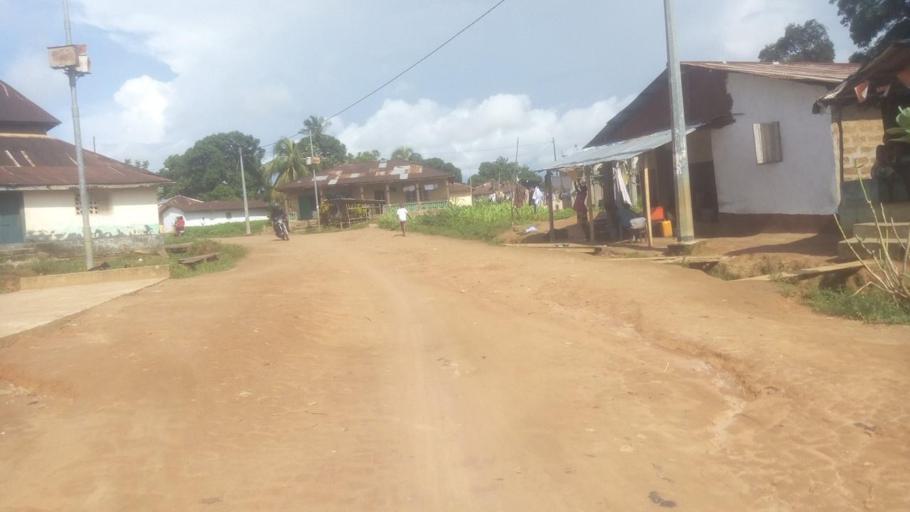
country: SL
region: Northern Province
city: Masoyila
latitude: 8.6109
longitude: -13.1919
